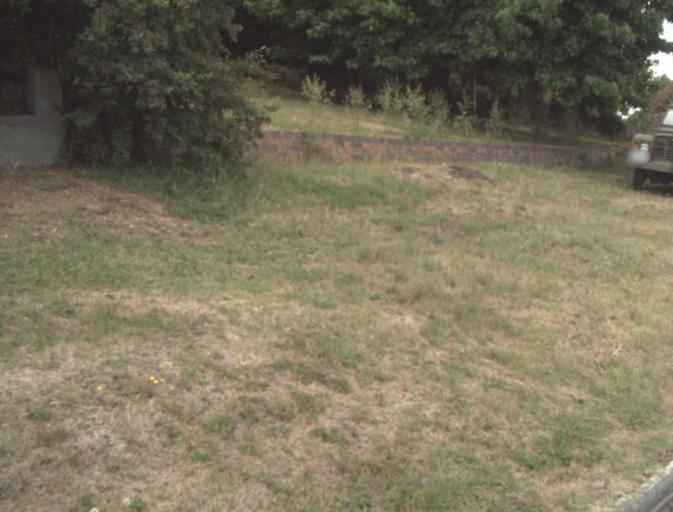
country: AU
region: Tasmania
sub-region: Launceston
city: Launceston
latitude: -41.4278
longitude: 147.1156
